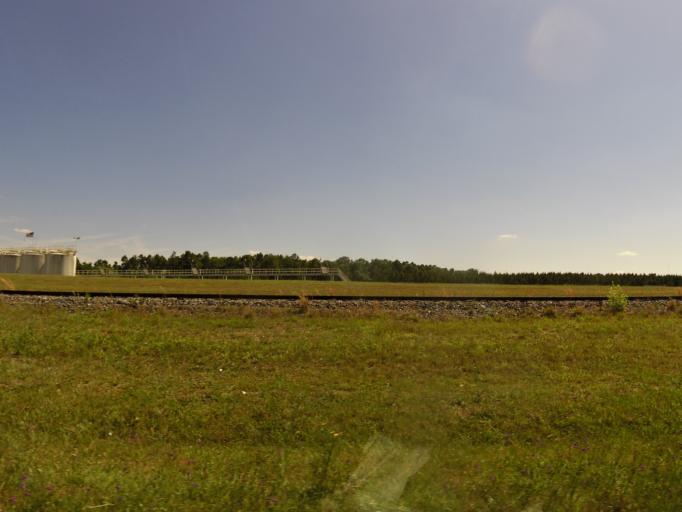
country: US
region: South Carolina
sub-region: Aiken County
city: Aiken
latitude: 33.5209
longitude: -81.6058
